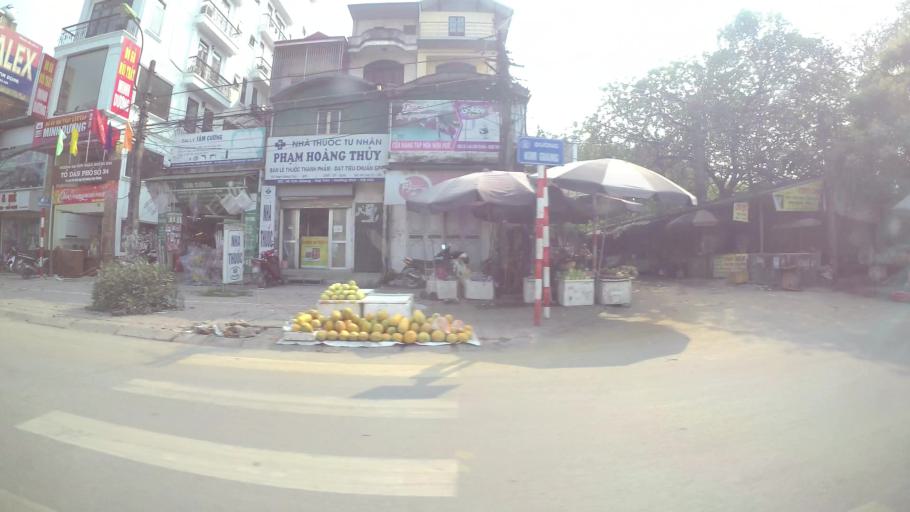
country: VN
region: Ha Noi
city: Thanh Xuan
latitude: 20.9830
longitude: 105.8154
